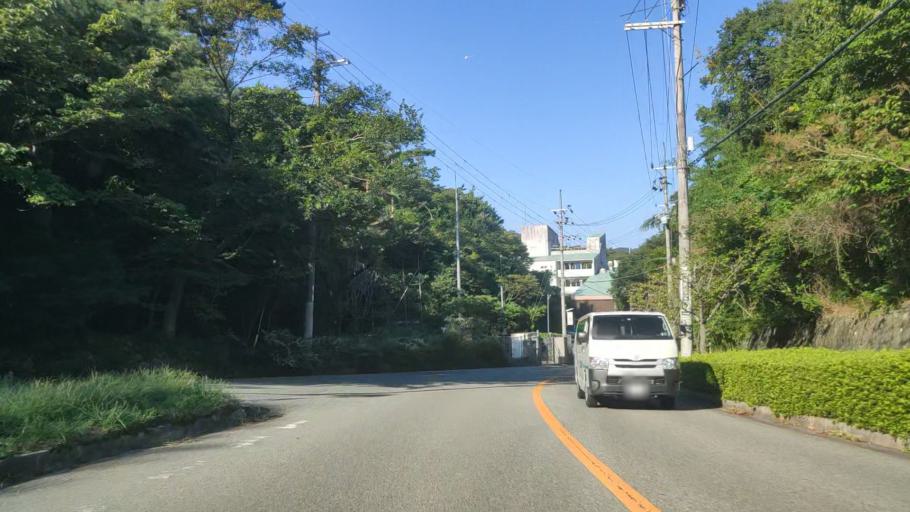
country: JP
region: Hyogo
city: Sandacho
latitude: 34.7982
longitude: 135.2422
